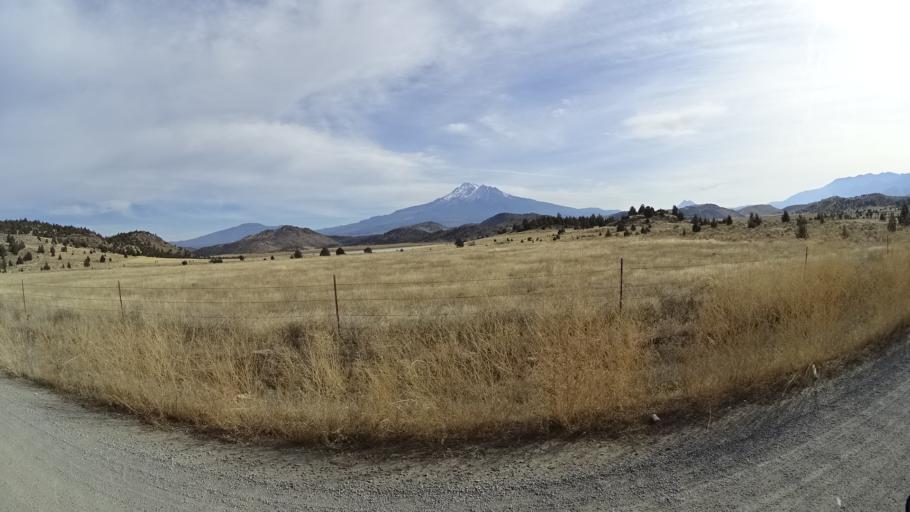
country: US
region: California
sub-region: Siskiyou County
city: Weed
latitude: 41.5623
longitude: -122.4689
